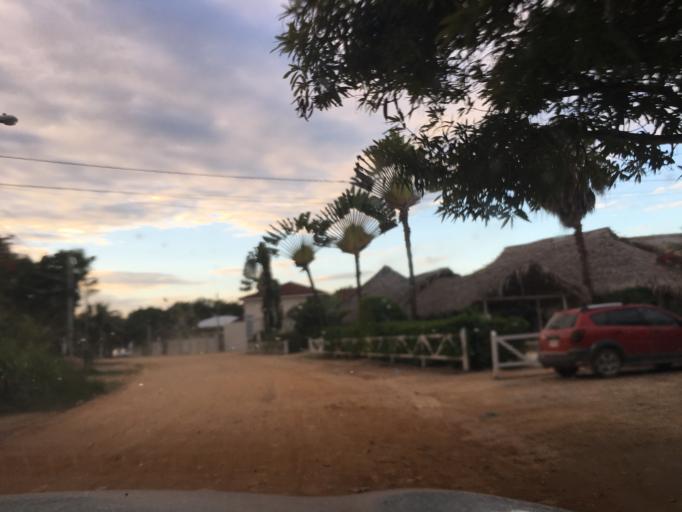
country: BZ
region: Stann Creek
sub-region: Dangriga
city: Dangriga
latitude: 16.8395
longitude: -88.2712
